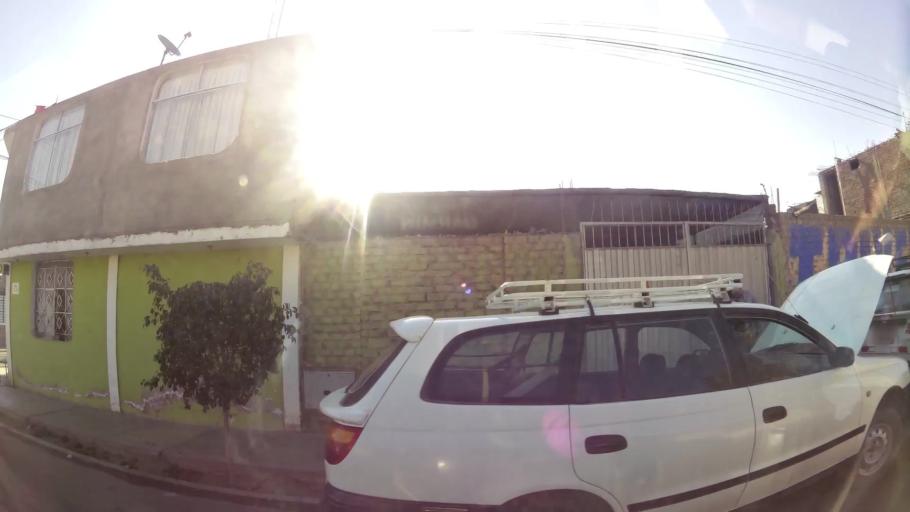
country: PE
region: Ica
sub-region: Provincia de Ica
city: La Tinguina
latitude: -14.0508
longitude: -75.6995
